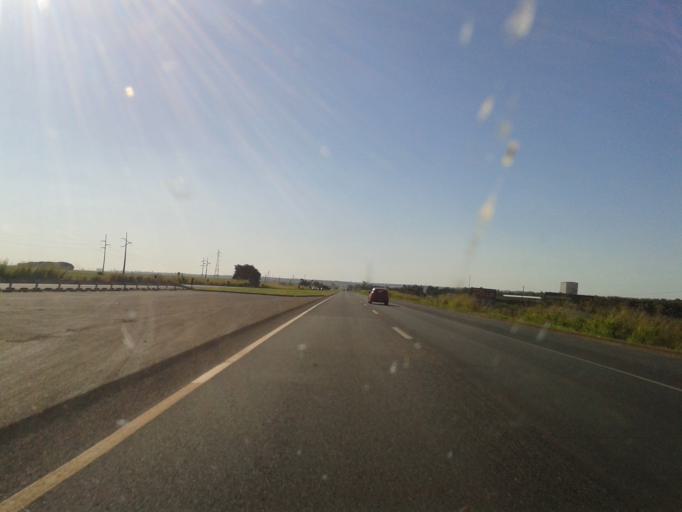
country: BR
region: Minas Gerais
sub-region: Uberlandia
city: Uberlandia
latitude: -19.0453
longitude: -48.1978
